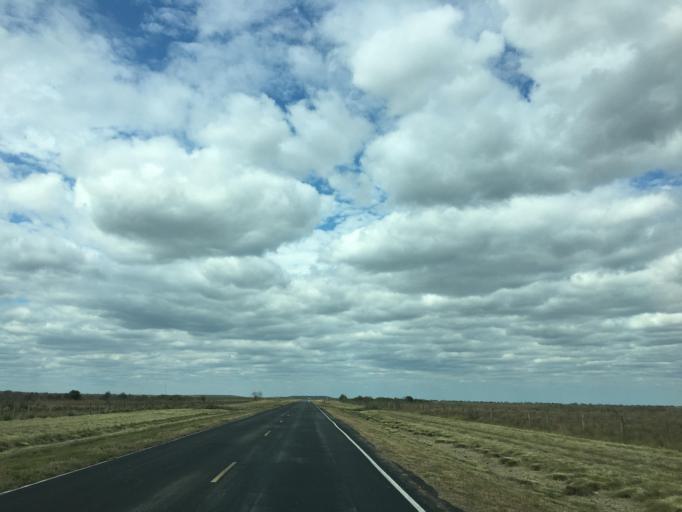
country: US
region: Texas
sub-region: Brazoria County
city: Oyster Creek
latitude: 29.0622
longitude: -95.2859
